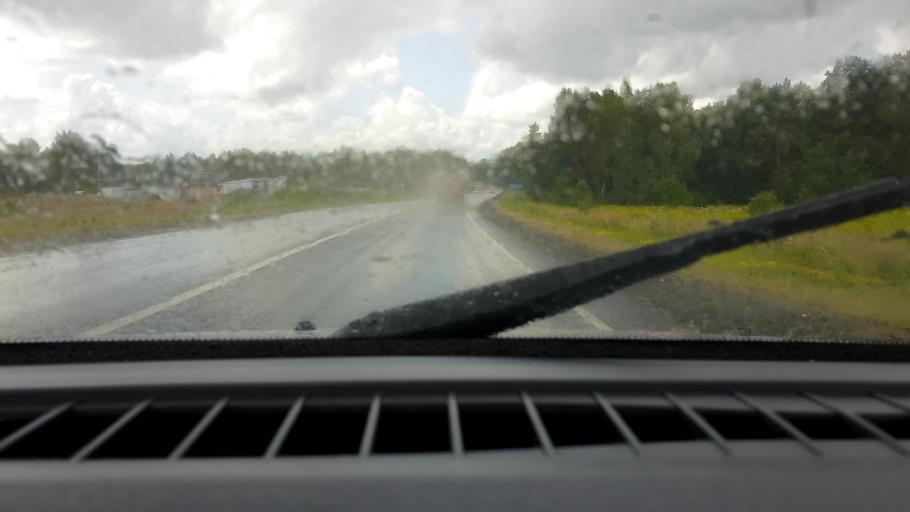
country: RU
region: Nizjnij Novgorod
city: Linda
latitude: 56.6684
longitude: 44.1386
